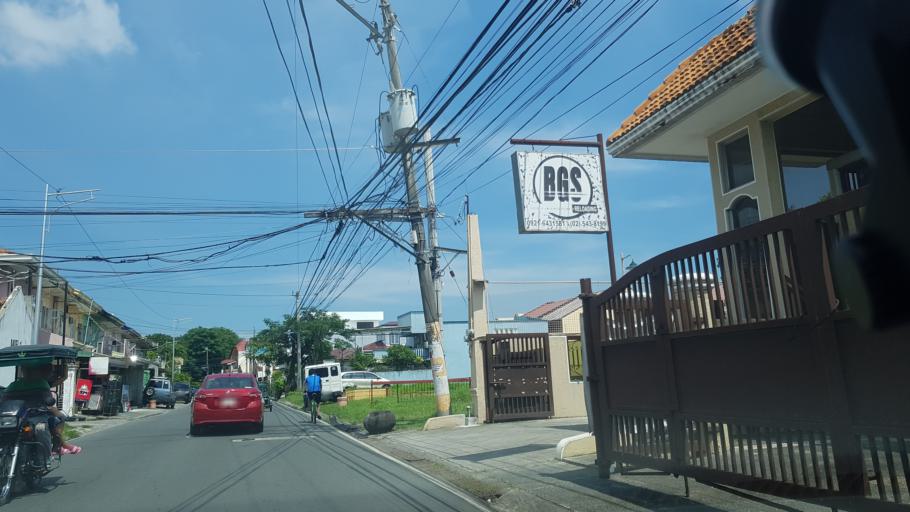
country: PH
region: Calabarzon
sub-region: Province of Rizal
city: Las Pinas
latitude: 14.4345
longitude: 120.9935
